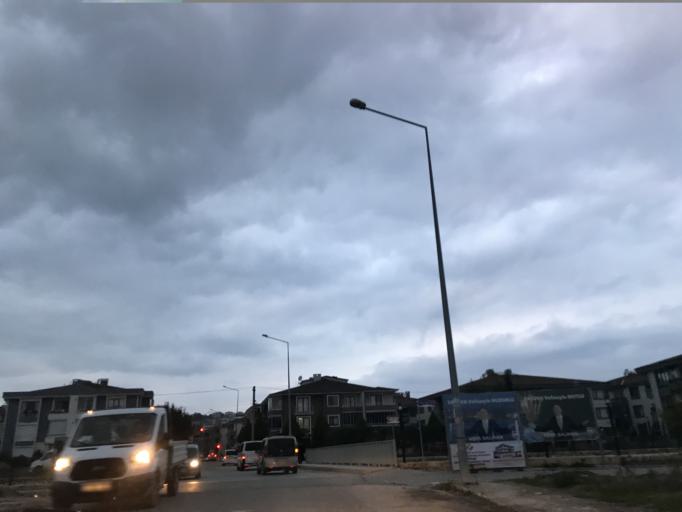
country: TR
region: Yalova
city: Yalova
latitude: 40.6409
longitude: 29.2602
